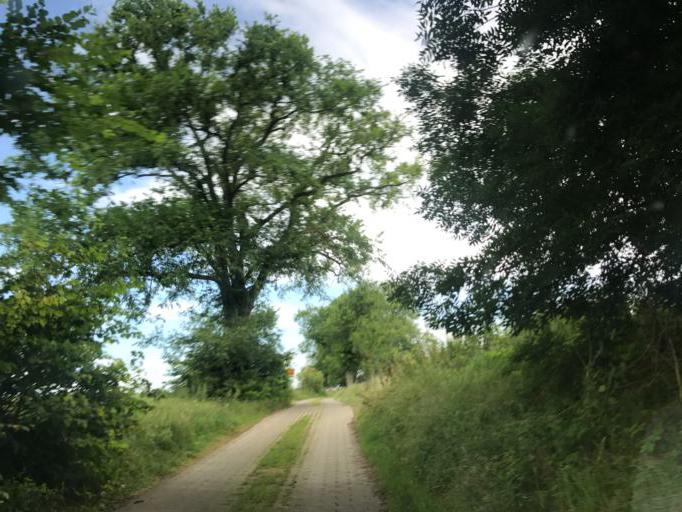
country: DE
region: Mecklenburg-Vorpommern
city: Mollenhagen
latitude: 53.4555
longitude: 12.9551
